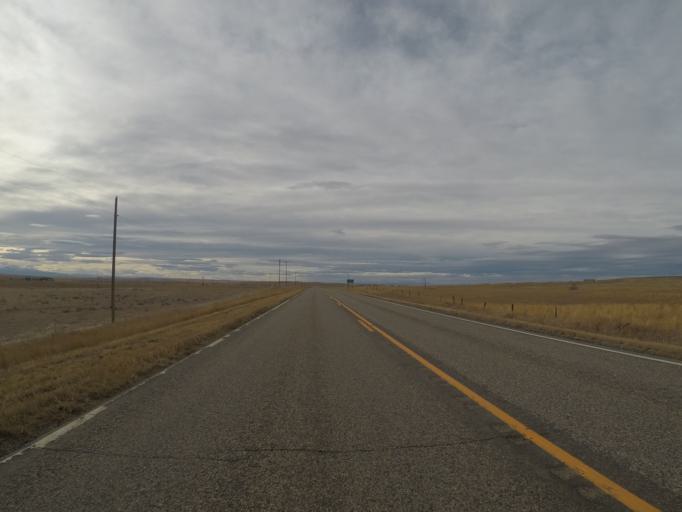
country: US
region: Montana
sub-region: Yellowstone County
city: Laurel
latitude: 45.8565
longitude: -108.8784
